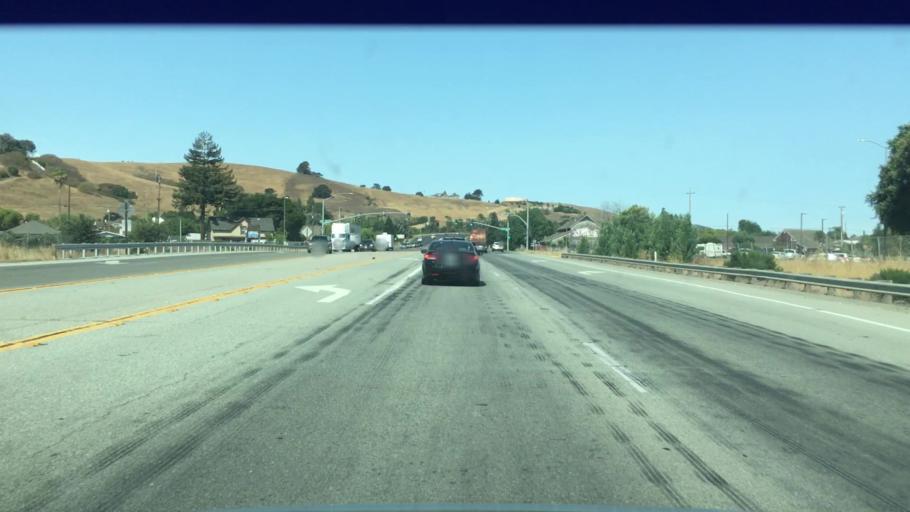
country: US
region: California
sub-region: San Benito County
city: San Juan Bautista
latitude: 36.8407
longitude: -121.5316
